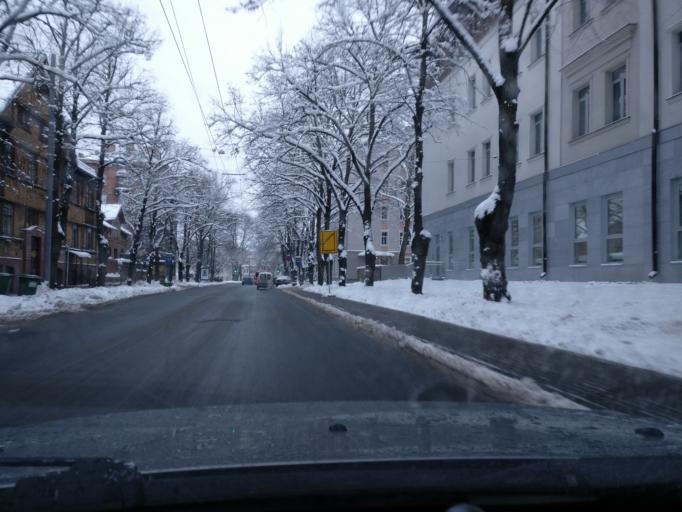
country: LV
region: Marupe
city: Marupe
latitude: 56.9315
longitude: 24.0704
